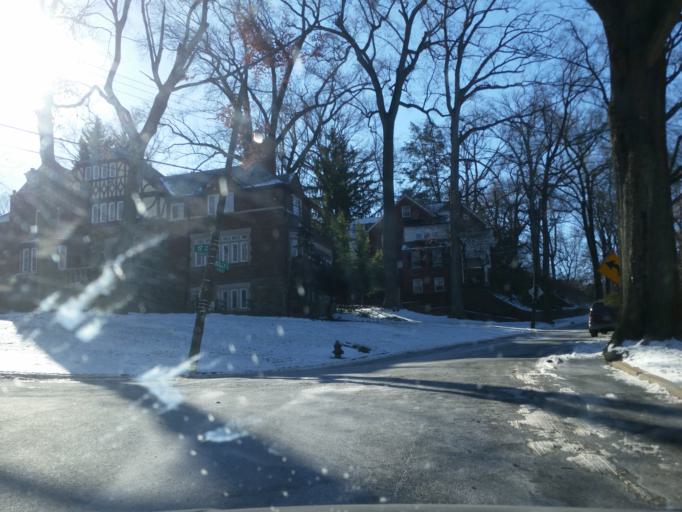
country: US
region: Maryland
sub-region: Montgomery County
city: Silver Spring
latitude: 38.9826
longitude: -77.0384
